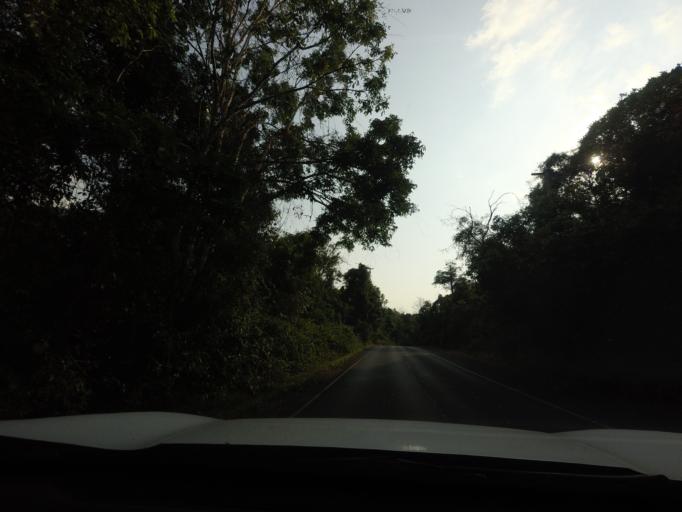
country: TH
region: Nakhon Nayok
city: Nakhon Nayok
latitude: 14.4134
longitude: 101.3781
